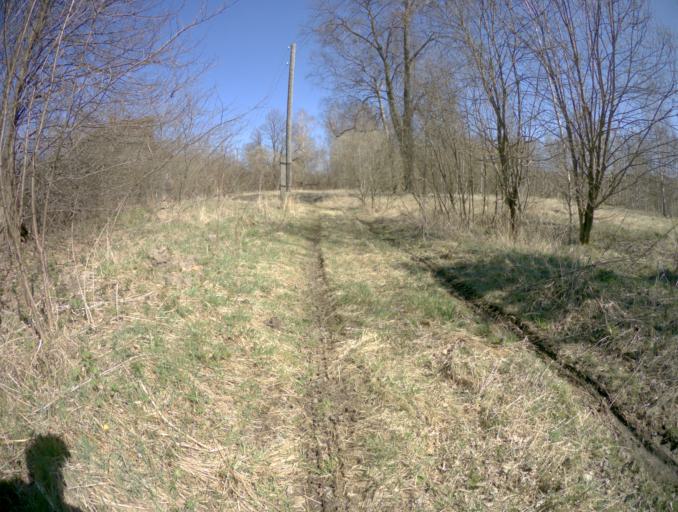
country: RU
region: Vladimir
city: Ivanishchi
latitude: 55.8648
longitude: 40.4360
